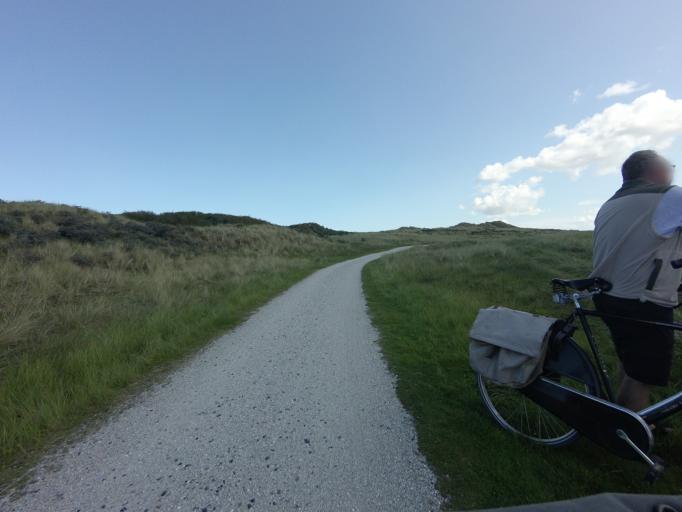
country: NL
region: Friesland
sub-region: Gemeente Terschelling
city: West-Terschelling
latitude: 53.4075
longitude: 5.3020
